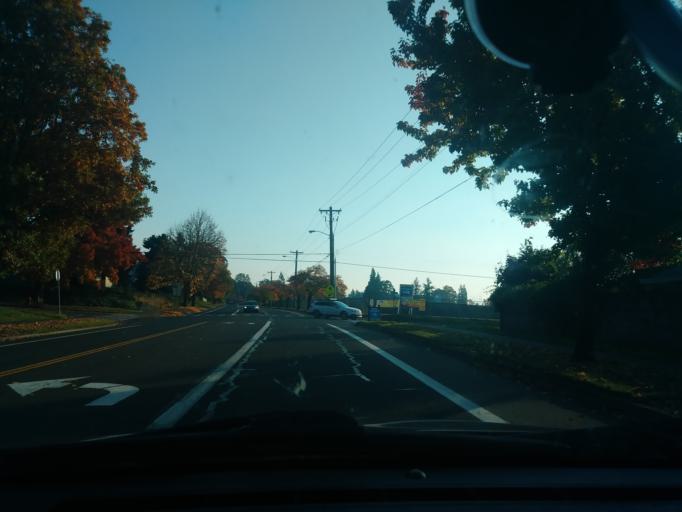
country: US
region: Oregon
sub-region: Washington County
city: Forest Grove
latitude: 45.5243
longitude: -123.1216
